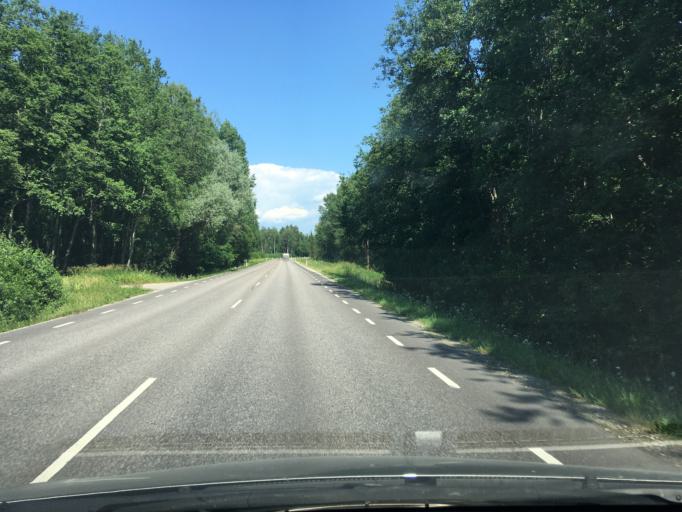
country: EE
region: Raplamaa
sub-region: Rapla vald
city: Rapla
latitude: 58.9851
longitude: 24.7452
